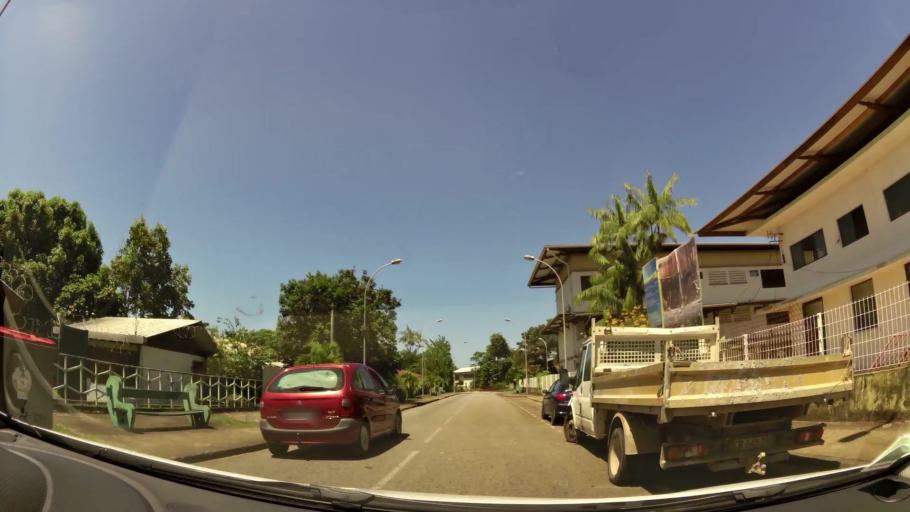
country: GF
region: Guyane
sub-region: Guyane
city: Cayenne
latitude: 4.9428
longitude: -52.3204
